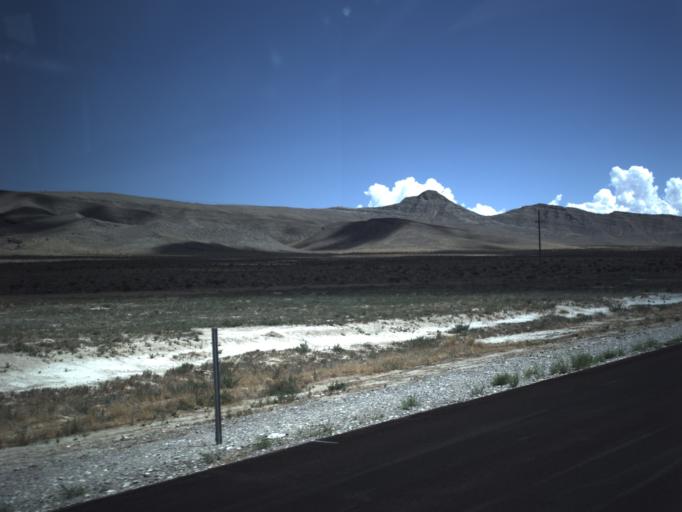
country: US
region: Utah
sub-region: Beaver County
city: Milford
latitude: 39.0492
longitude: -113.4171
